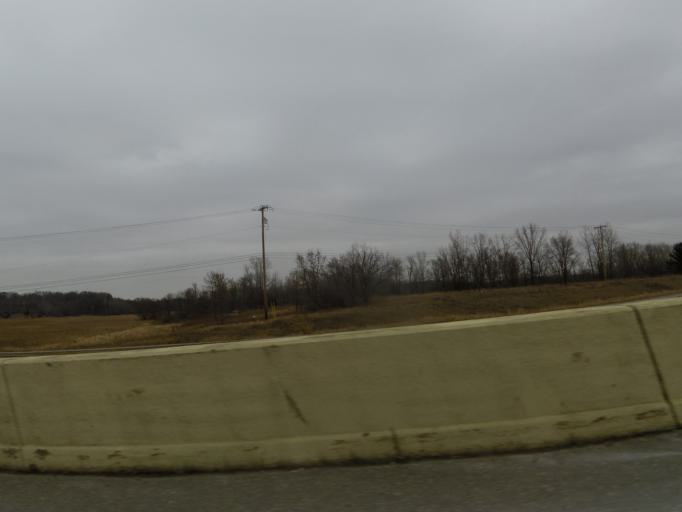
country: US
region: Minnesota
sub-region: Hennepin County
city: Orono
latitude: 44.9937
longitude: -93.6209
